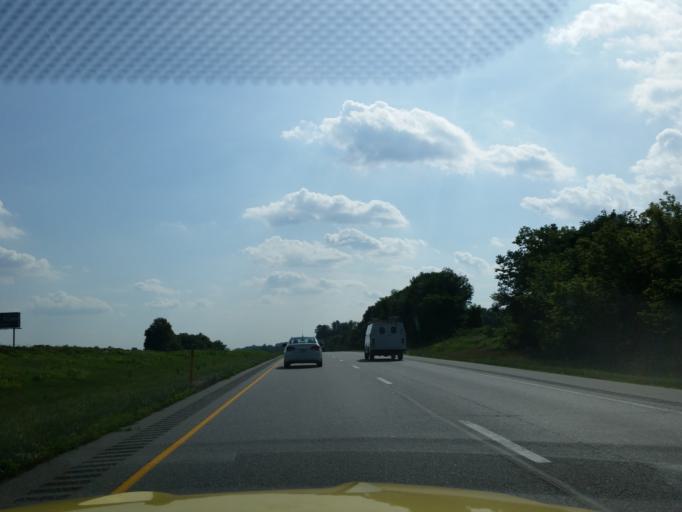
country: US
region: Pennsylvania
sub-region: Lancaster County
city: Marietta
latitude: 40.0238
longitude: -76.5679
